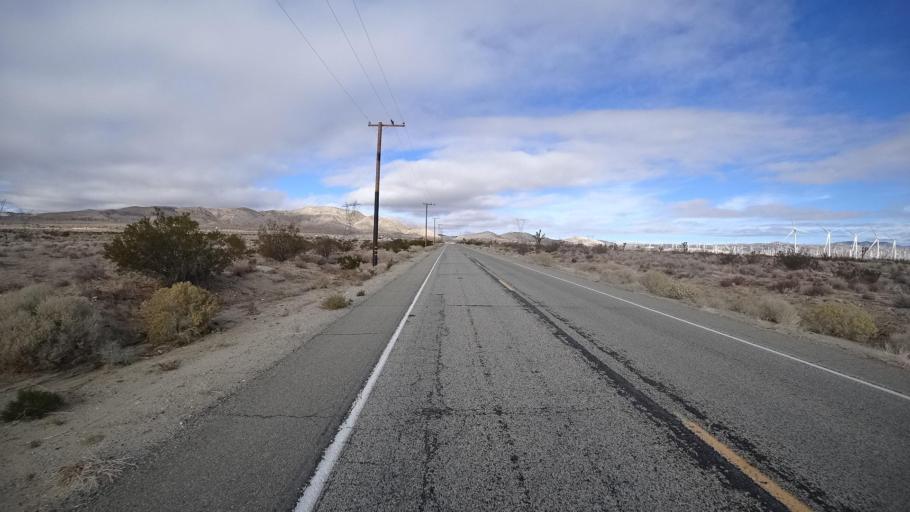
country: US
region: California
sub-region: Kern County
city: Mojave
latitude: 34.9860
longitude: -118.3194
